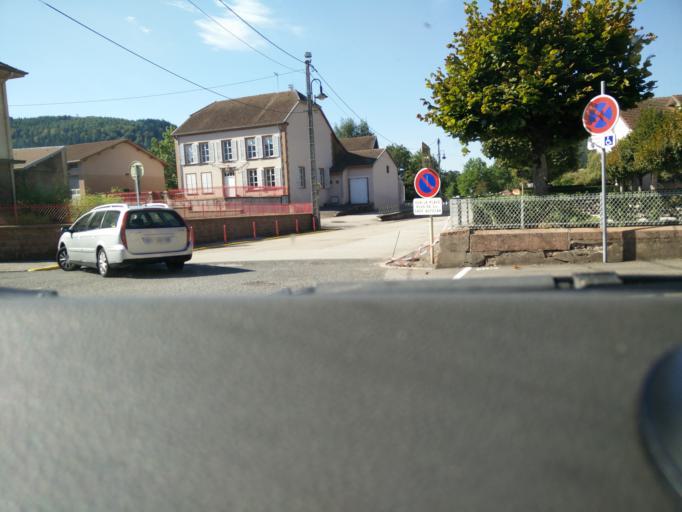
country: FR
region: Lorraine
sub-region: Departement des Vosges
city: Senones
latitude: 48.4559
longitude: 6.9489
